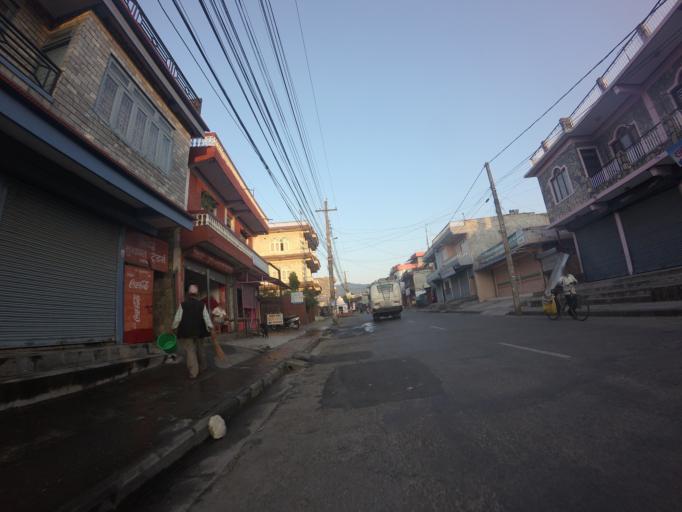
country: NP
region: Western Region
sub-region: Gandaki Zone
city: Pokhara
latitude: 28.2203
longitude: 83.9973
